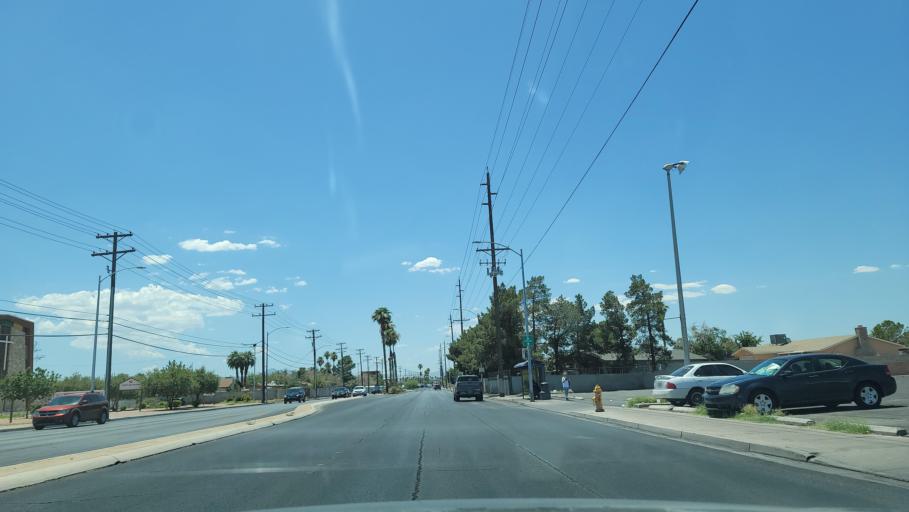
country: US
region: Nevada
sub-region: Clark County
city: North Las Vegas
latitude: 36.1847
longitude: -115.1162
